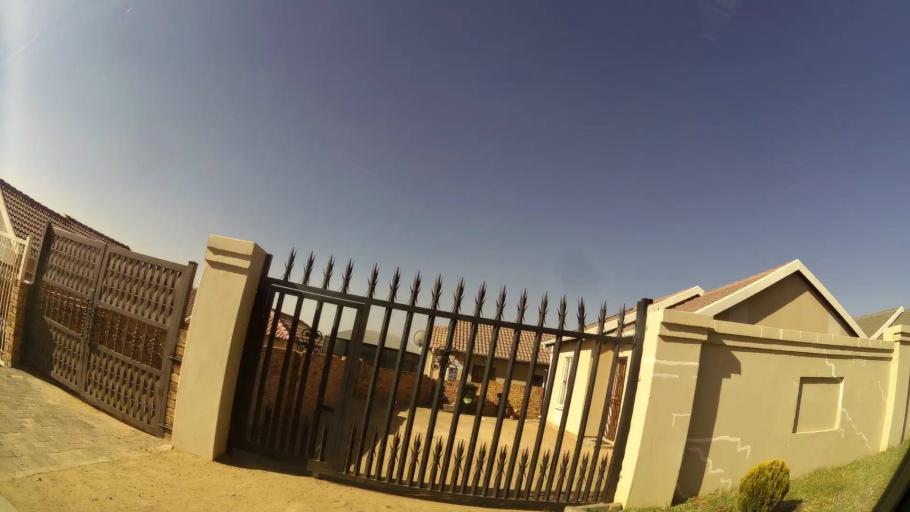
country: ZA
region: Gauteng
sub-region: West Rand District Municipality
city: Muldersdriseloop
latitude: -26.0120
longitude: 27.9403
